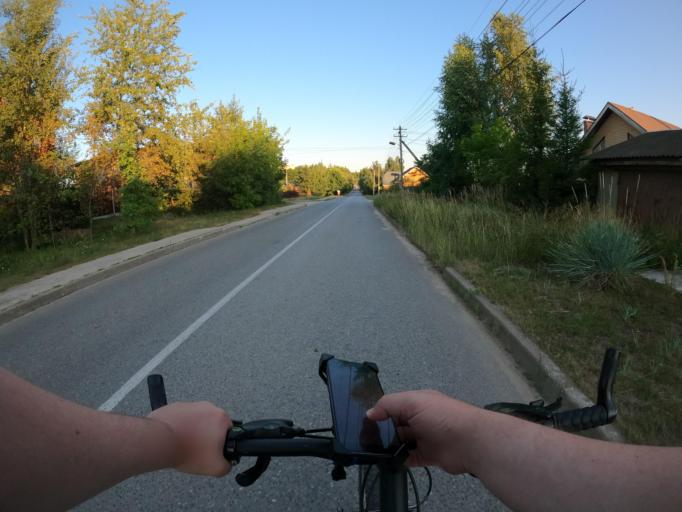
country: RU
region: Moskovskaya
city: Beloozerskiy
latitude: 55.4646
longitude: 38.4301
